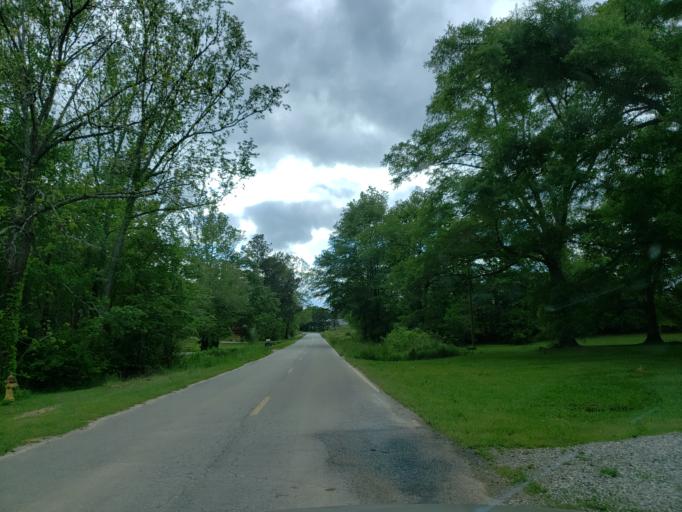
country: US
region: Georgia
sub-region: Haralson County
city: Tallapoosa
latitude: 33.7744
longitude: -85.3541
